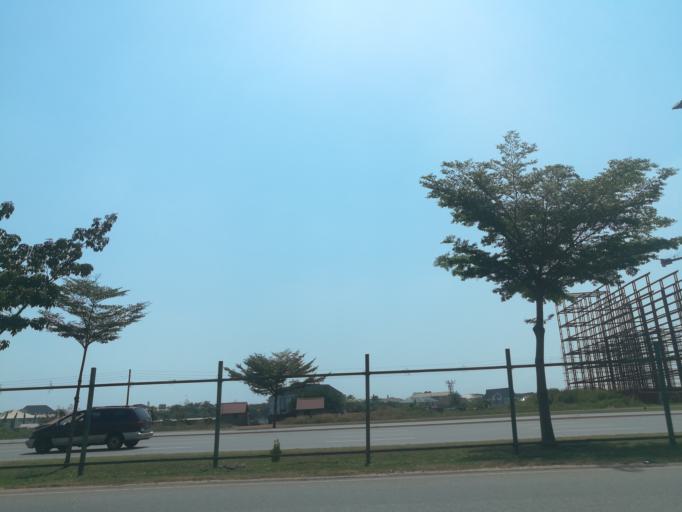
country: NG
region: Abuja Federal Capital Territory
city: Abuja
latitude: 9.0772
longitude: 7.4457
